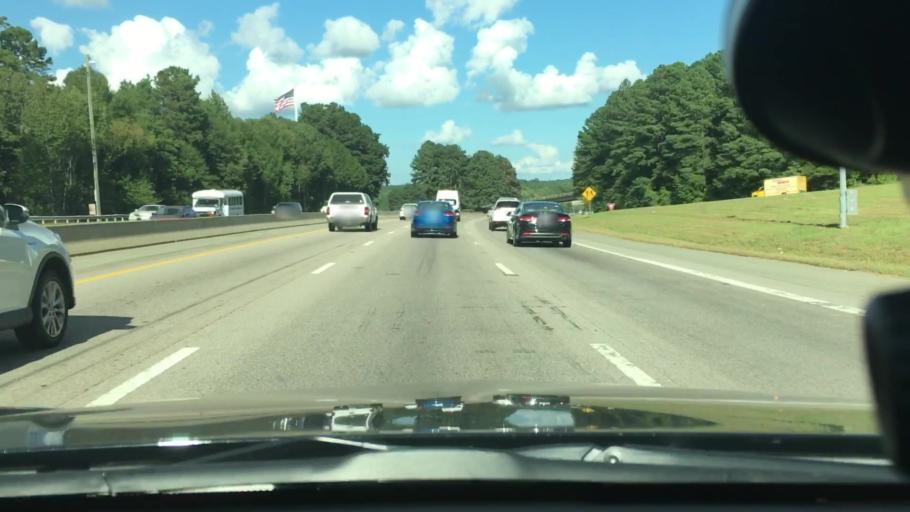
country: US
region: North Carolina
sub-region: Wake County
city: West Raleigh
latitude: 35.8326
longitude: -78.6759
